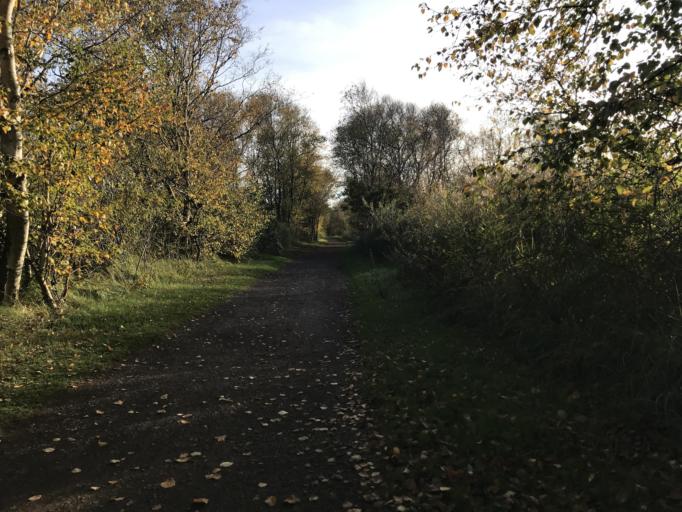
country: DE
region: Lower Saxony
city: Borkum
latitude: 53.5755
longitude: 6.7074
